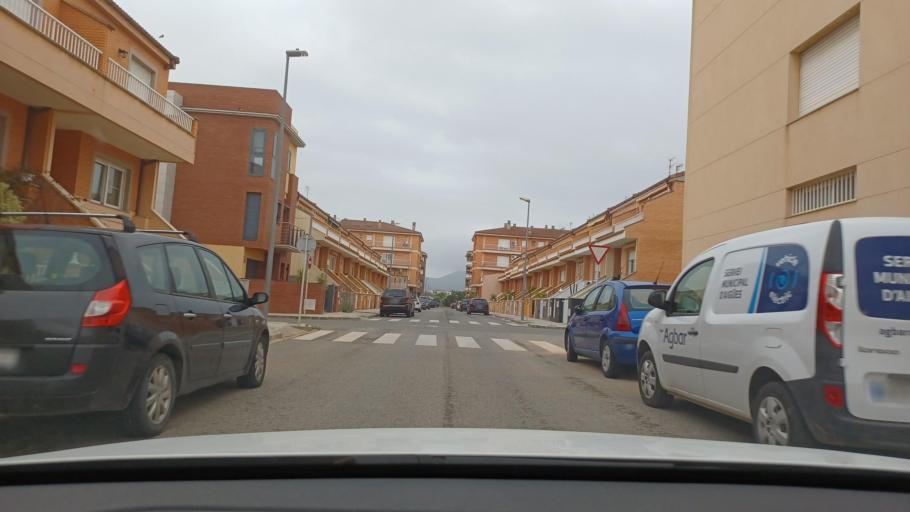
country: ES
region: Catalonia
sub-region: Provincia de Tarragona
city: Amposta
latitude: 40.7054
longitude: 0.5729
